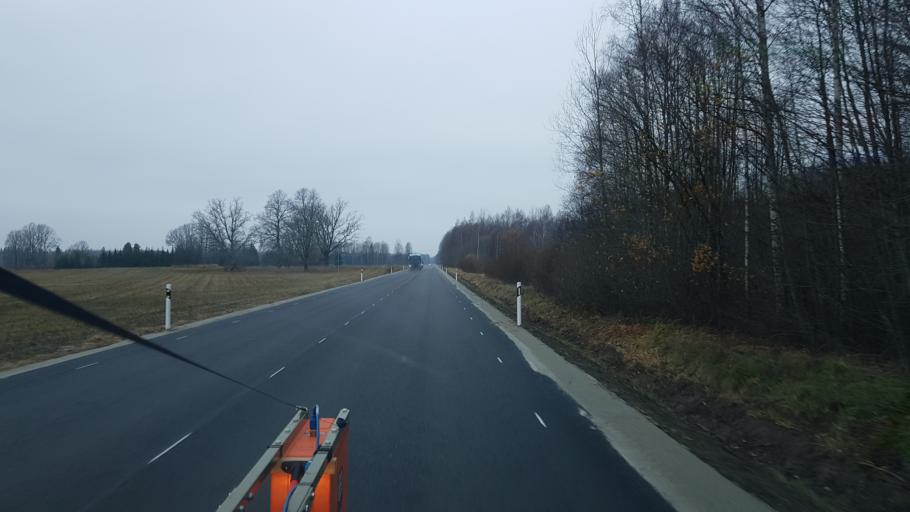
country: EE
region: Paernumaa
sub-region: Vaendra vald (alev)
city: Vandra
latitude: 58.8354
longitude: 25.0854
